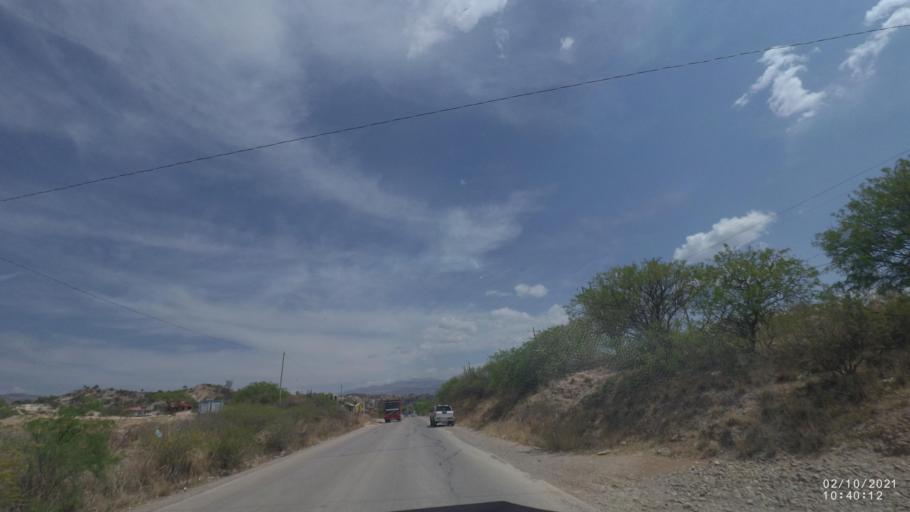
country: BO
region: Cochabamba
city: Capinota
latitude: -17.6239
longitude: -66.2834
